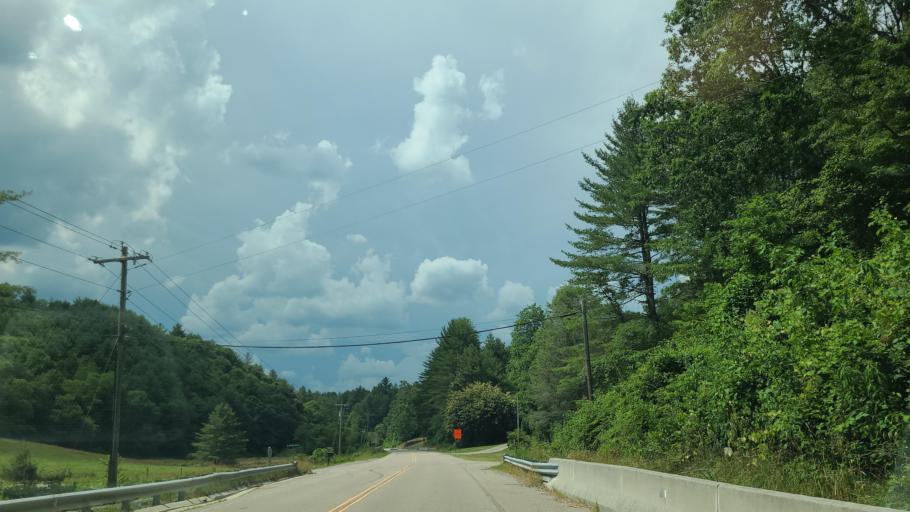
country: US
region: North Carolina
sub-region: Ashe County
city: Jefferson
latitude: 36.3659
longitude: -81.3906
